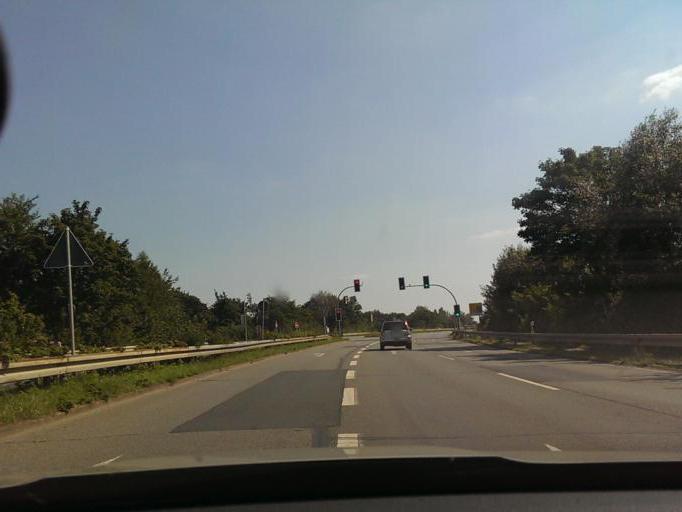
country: DE
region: Lower Saxony
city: Langenhagen
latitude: 52.4284
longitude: 9.7731
